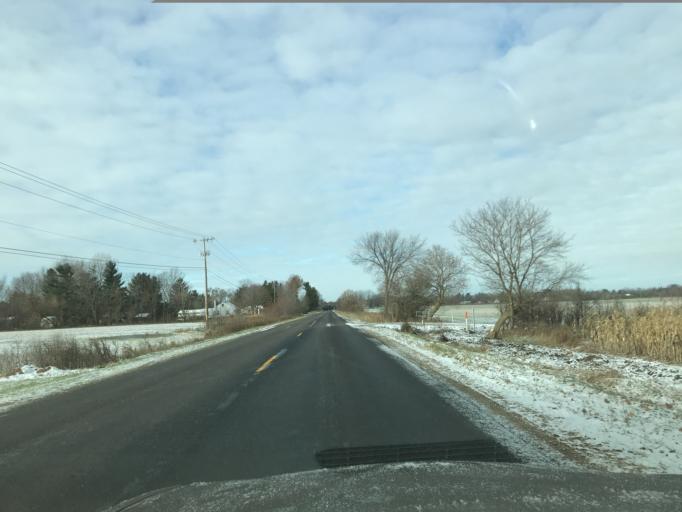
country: US
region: Michigan
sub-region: Eaton County
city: Dimondale
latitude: 42.6402
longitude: -84.6266
